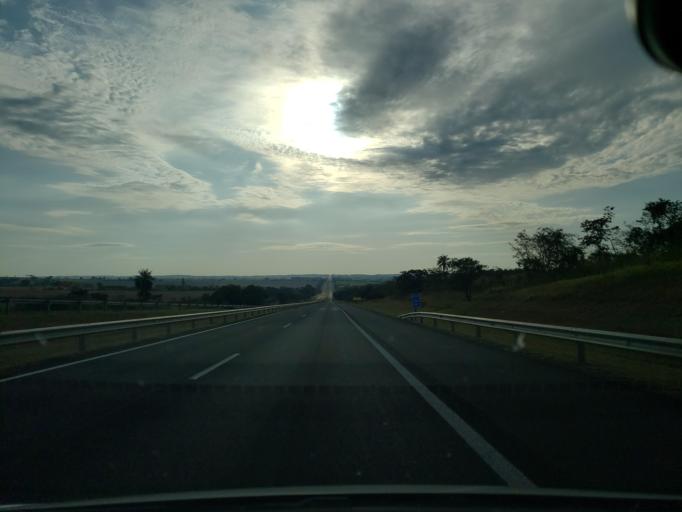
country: BR
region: Sao Paulo
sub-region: Mirandopolis
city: Mirandopolis
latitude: -21.1078
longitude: -51.0285
